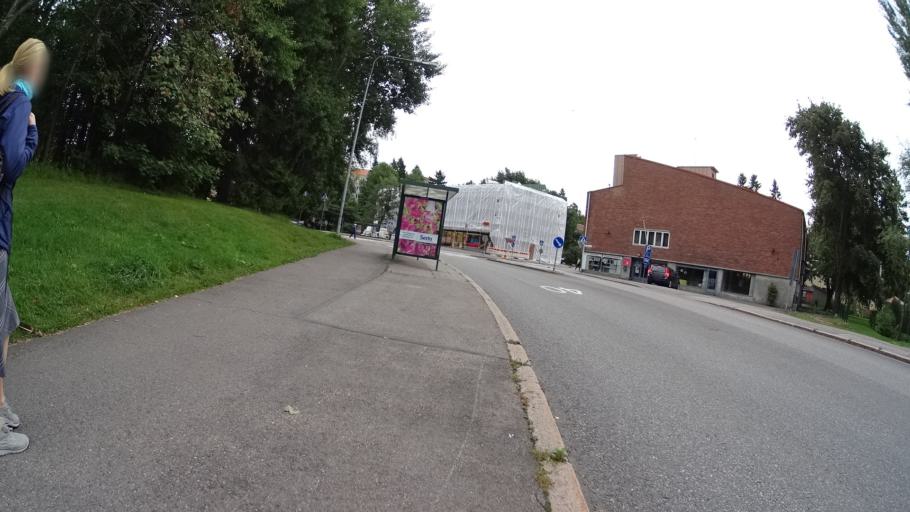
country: FI
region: Uusimaa
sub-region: Helsinki
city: Helsinki
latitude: 60.2281
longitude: 24.9254
